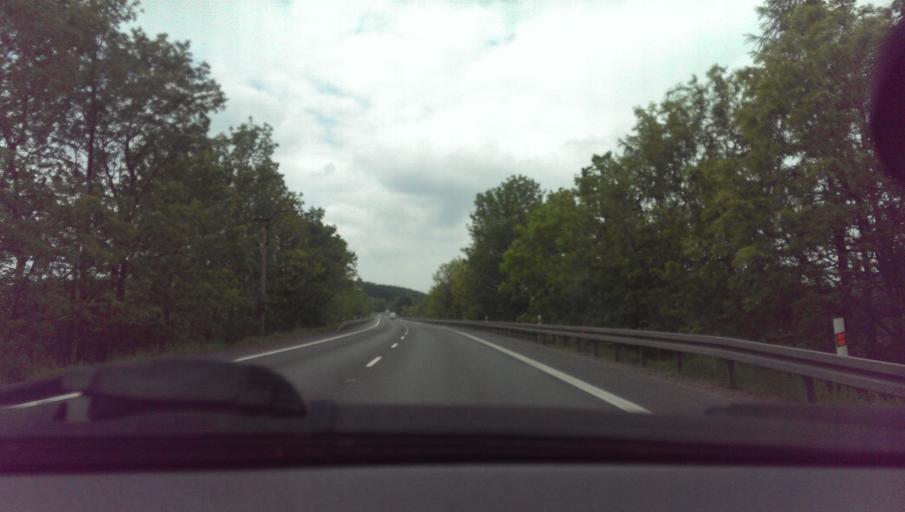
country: CZ
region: Zlin
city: Buchlovice
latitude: 49.0909
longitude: 17.3257
